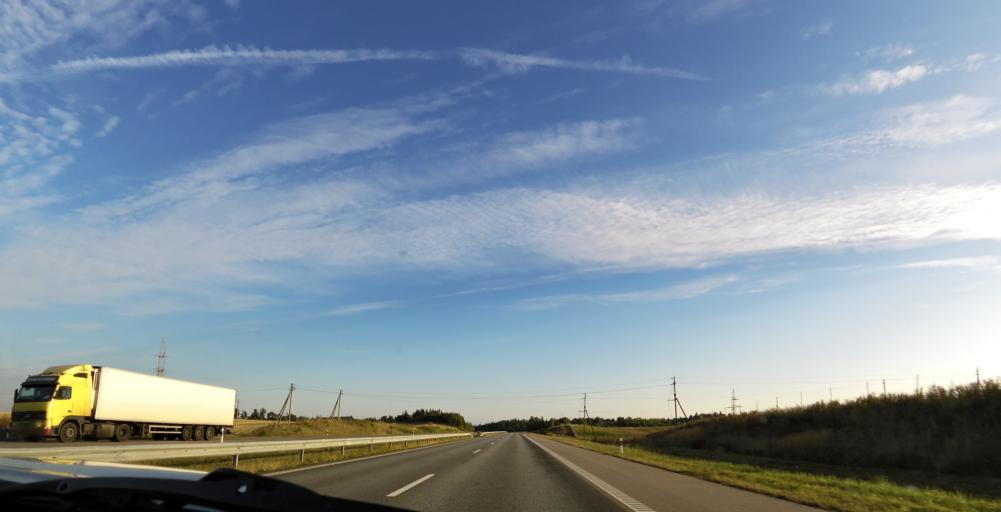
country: LT
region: Vilnius County
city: Ukmerge
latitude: 55.2029
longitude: 24.8156
